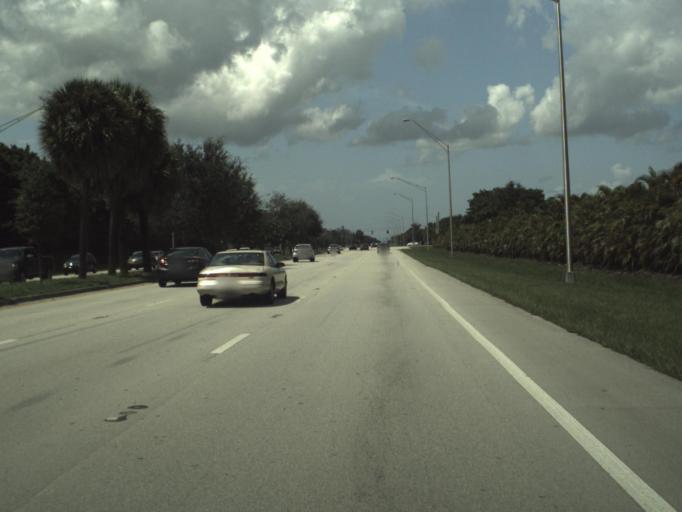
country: US
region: Florida
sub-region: Palm Beach County
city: Boca Pointe
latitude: 26.3796
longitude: -80.2035
